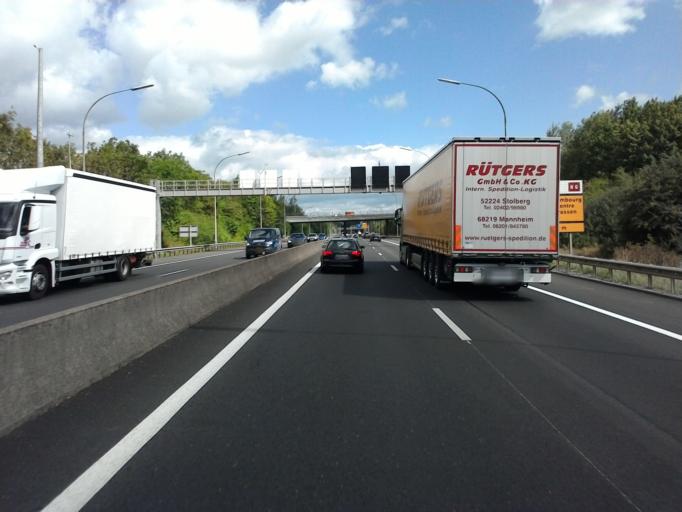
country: LU
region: Luxembourg
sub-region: Canton de Luxembourg
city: Strassen
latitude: 49.6107
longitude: 6.0820
